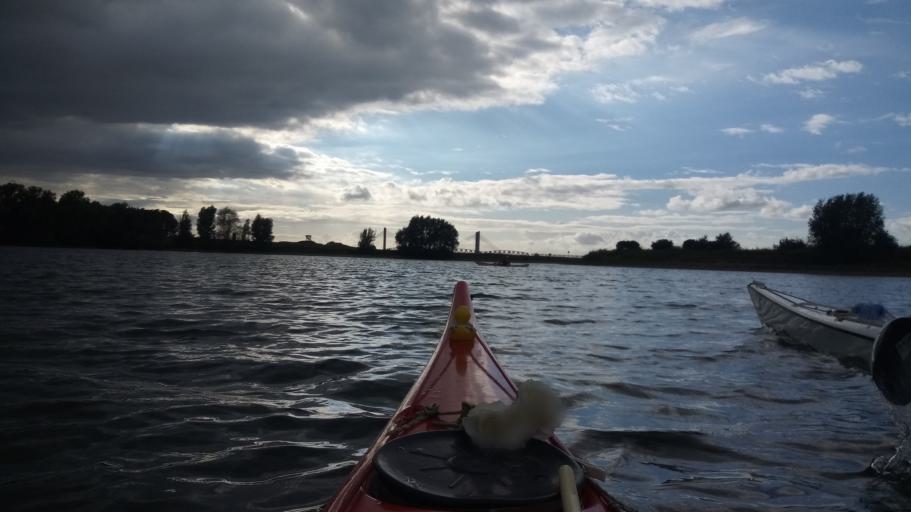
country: NL
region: Gelderland
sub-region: Gemeente Neerijnen
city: Neerijnen
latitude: 51.8186
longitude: 5.2891
